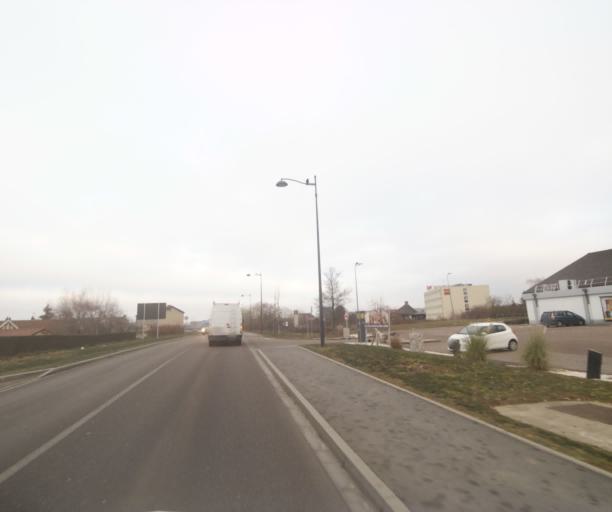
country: FR
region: Champagne-Ardenne
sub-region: Departement de la Haute-Marne
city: Bettancourt-la-Ferree
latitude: 48.6482
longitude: 4.9563
